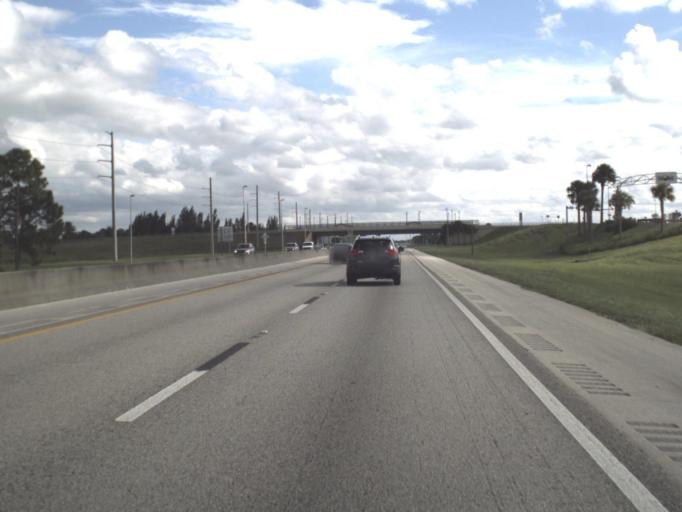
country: US
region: Florida
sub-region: Martin County
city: North River Shores
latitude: 27.2127
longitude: -80.3353
